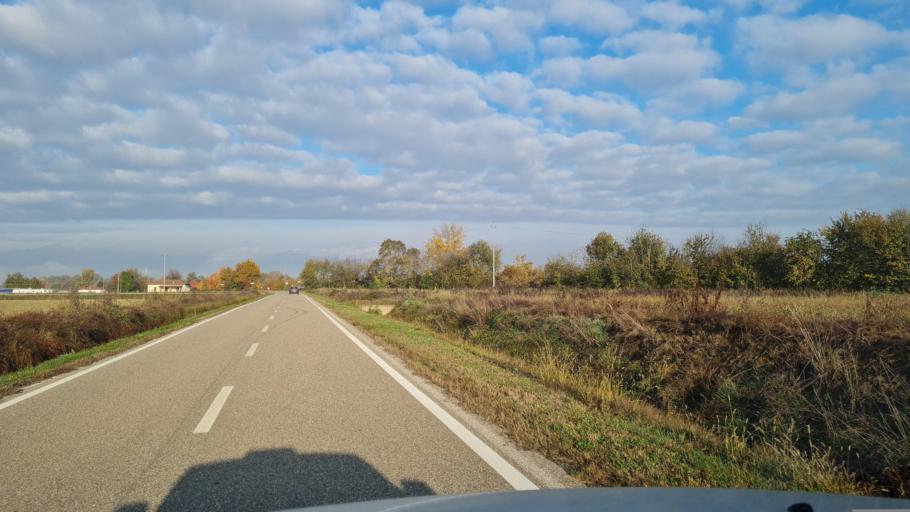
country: IT
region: Piedmont
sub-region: Provincia di Vercelli
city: Villarboit
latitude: 45.4429
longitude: 8.3314
